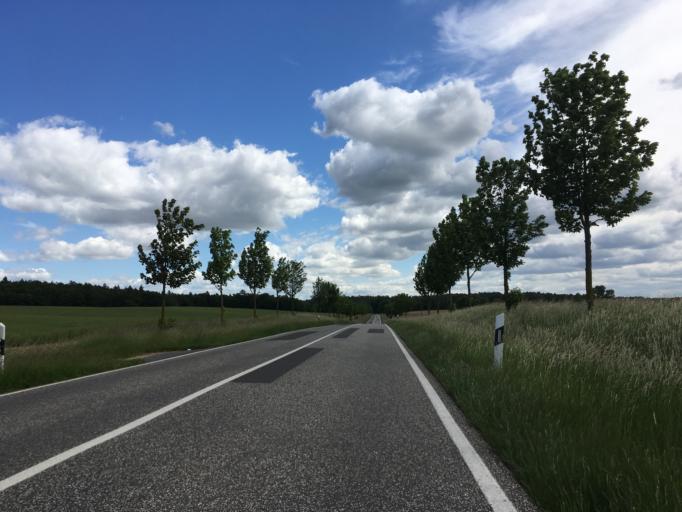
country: DE
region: Brandenburg
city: Protzel
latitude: 52.7114
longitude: 14.0084
